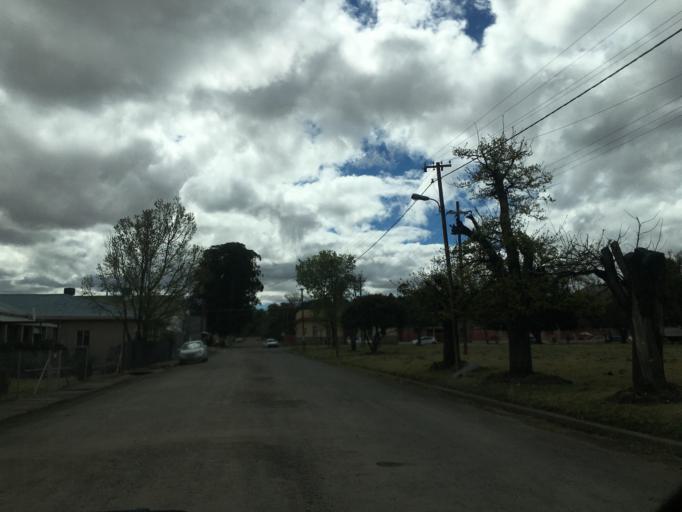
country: ZA
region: Eastern Cape
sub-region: Chris Hani District Municipality
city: Elliot
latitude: -31.3349
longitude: 27.8498
